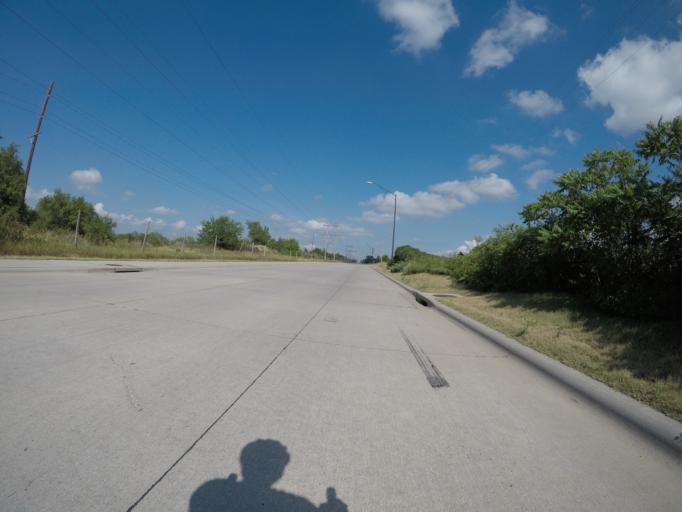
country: US
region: Nebraska
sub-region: Buffalo County
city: Kearney
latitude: 40.6708
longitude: -99.0789
